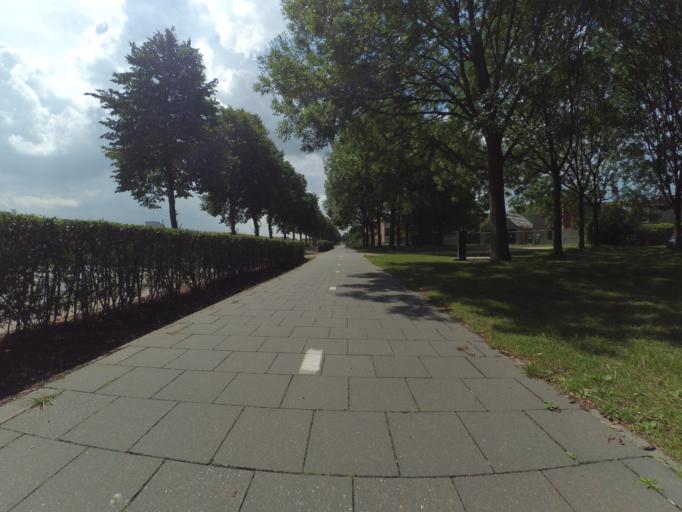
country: NL
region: Limburg
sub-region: Gemeente Maasgouw
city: Maasbracht
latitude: 51.1704
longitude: 5.8967
